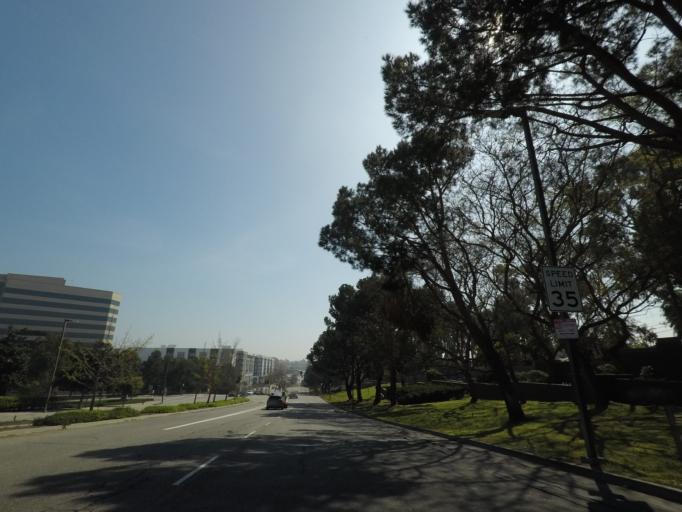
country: US
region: California
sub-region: Los Angeles County
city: Ladera Heights
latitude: 33.9748
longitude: -118.3927
